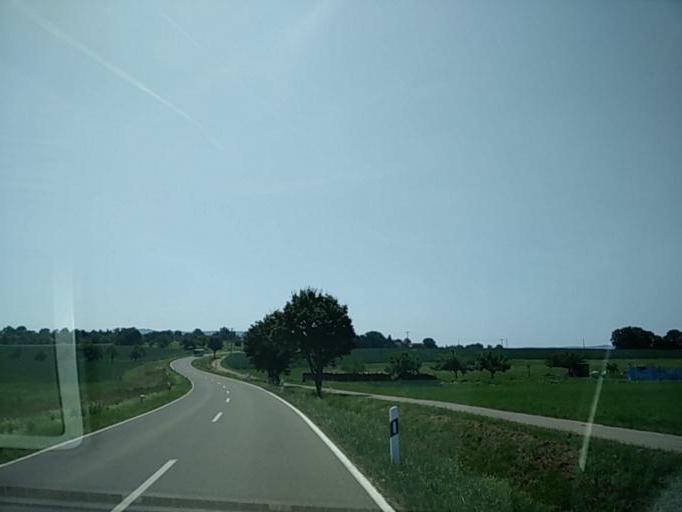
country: DE
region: Baden-Wuerttemberg
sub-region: Tuebingen Region
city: Gomaringen
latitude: 48.4689
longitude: 9.0886
